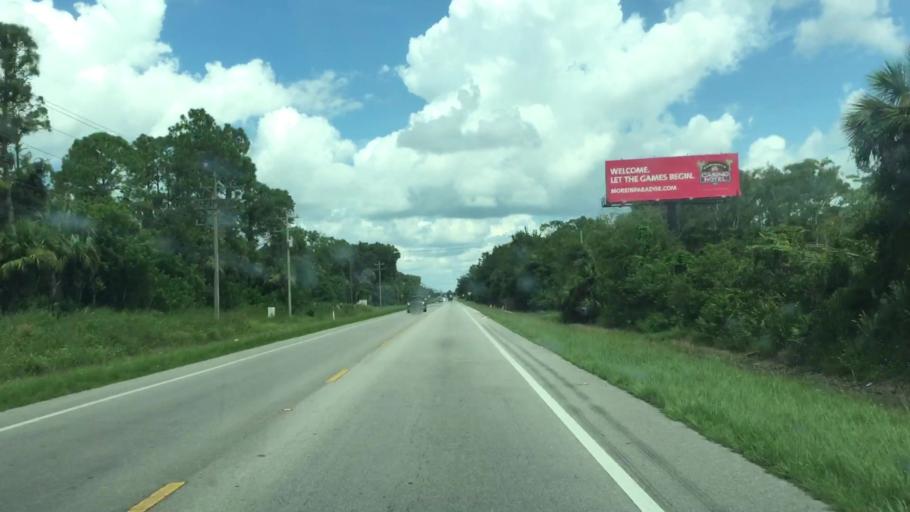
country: US
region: Florida
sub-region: Collier County
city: Immokalee
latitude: 26.4016
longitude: -81.4171
